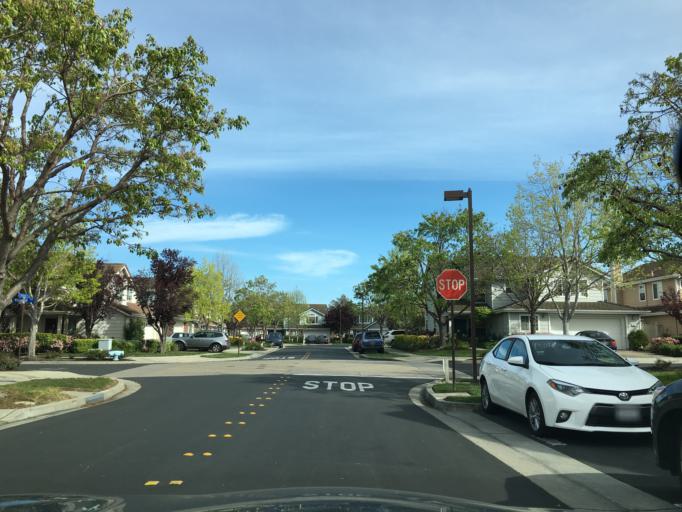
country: US
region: California
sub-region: San Mateo County
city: Redwood Shores
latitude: 37.5419
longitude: -122.2393
